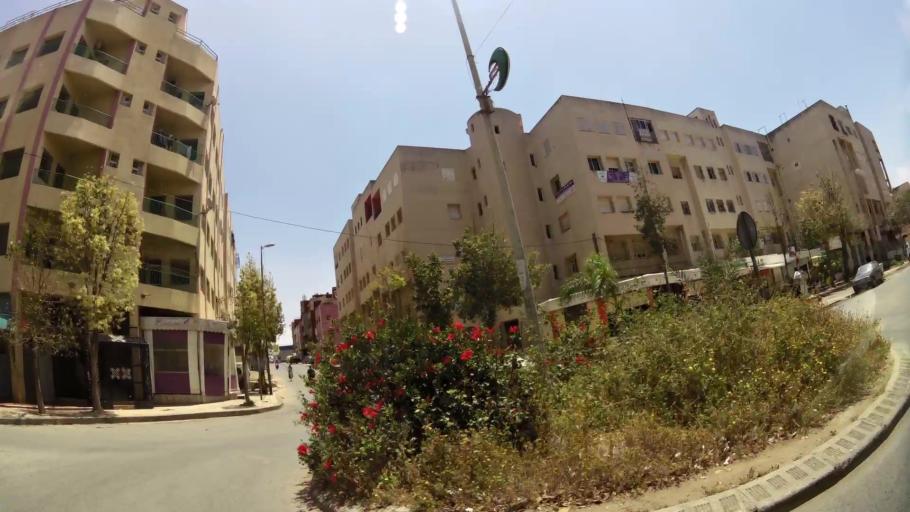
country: MA
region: Rabat-Sale-Zemmour-Zaer
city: Sale
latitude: 34.0598
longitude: -6.7959
